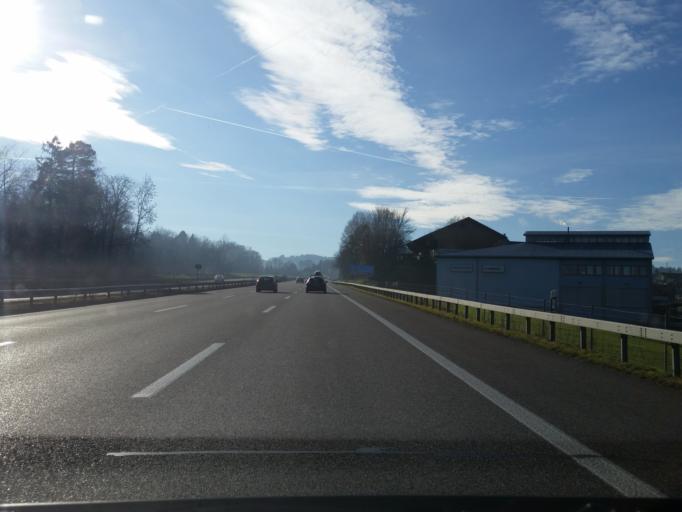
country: CH
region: Saint Gallen
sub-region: Wahlkreis Rorschach
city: Morschwil
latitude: 47.4642
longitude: 9.4386
